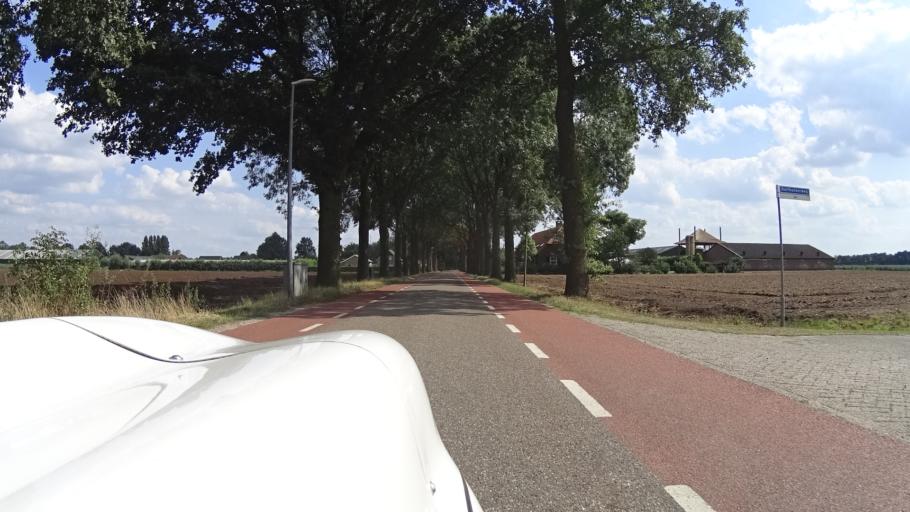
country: NL
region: North Brabant
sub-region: Gemeente Veghel
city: Mariaheide
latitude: 51.6408
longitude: 5.5915
